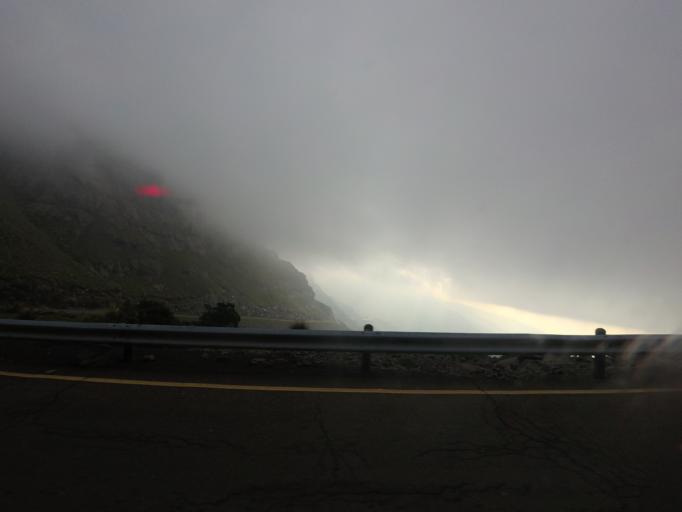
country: LS
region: Butha-Buthe
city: Butha-Buthe
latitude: -29.0627
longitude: 28.4025
